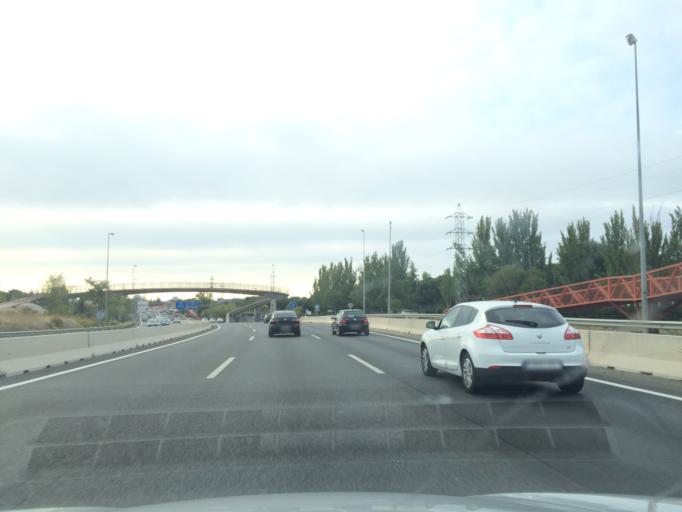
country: ES
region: Madrid
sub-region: Provincia de Madrid
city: Las Tablas
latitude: 40.5292
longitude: -3.6927
